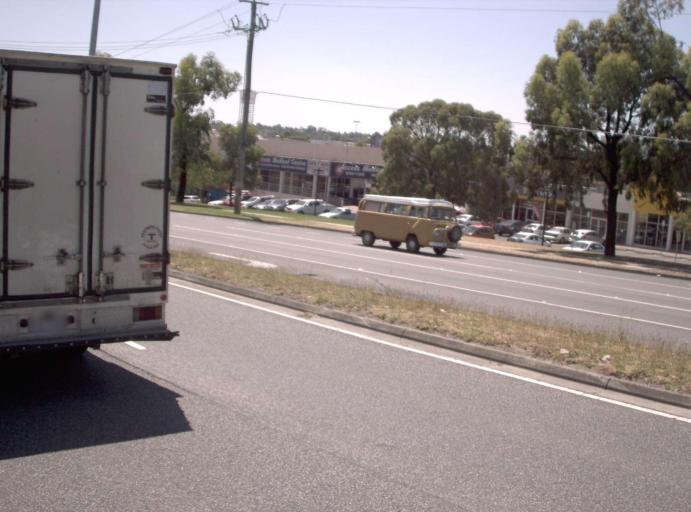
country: AU
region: Victoria
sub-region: Knox
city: Knoxfield
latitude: -37.8718
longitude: 145.2437
